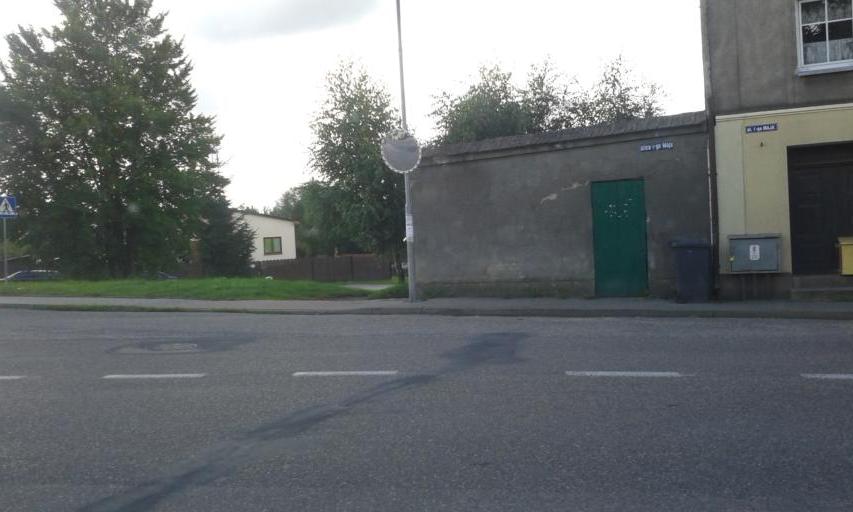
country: PL
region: West Pomeranian Voivodeship
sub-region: Powiat koszalinski
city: Bobolice
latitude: 53.9542
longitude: 16.5928
